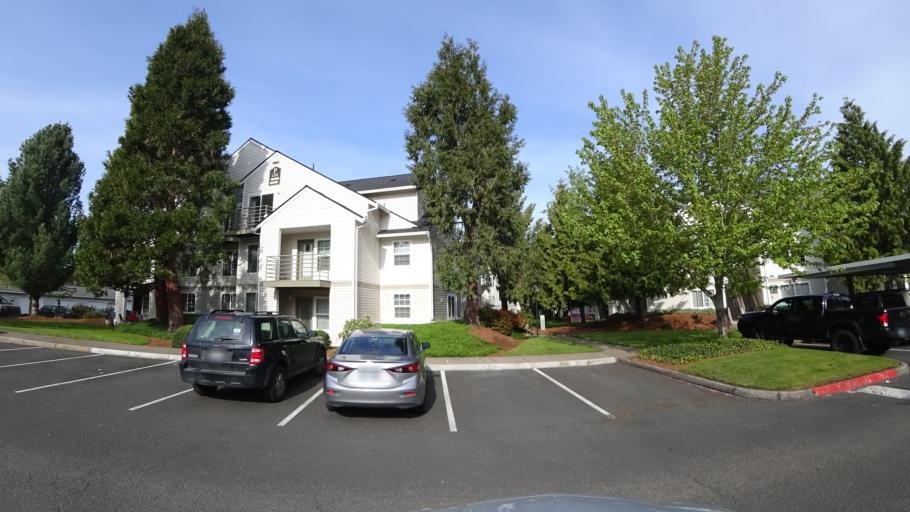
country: US
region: Oregon
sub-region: Washington County
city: Hillsboro
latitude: 45.5430
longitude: -122.9683
